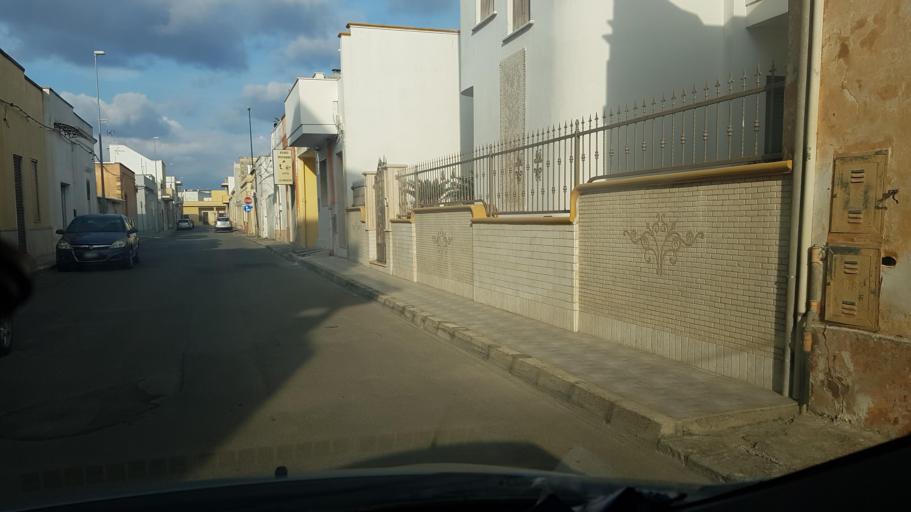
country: IT
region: Apulia
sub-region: Provincia di Lecce
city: Veglie
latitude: 40.3290
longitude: 17.9684
